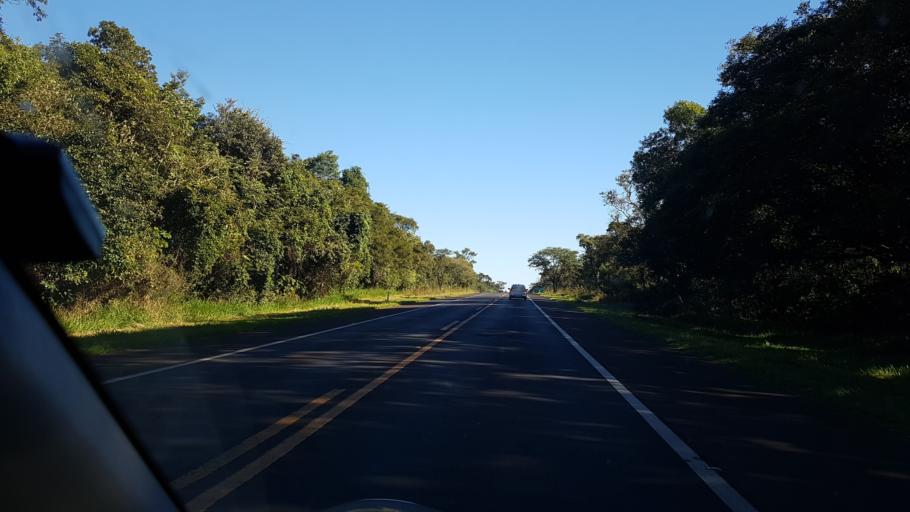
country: BR
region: Sao Paulo
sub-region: Assis
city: Assis
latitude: -22.6245
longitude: -50.4486
